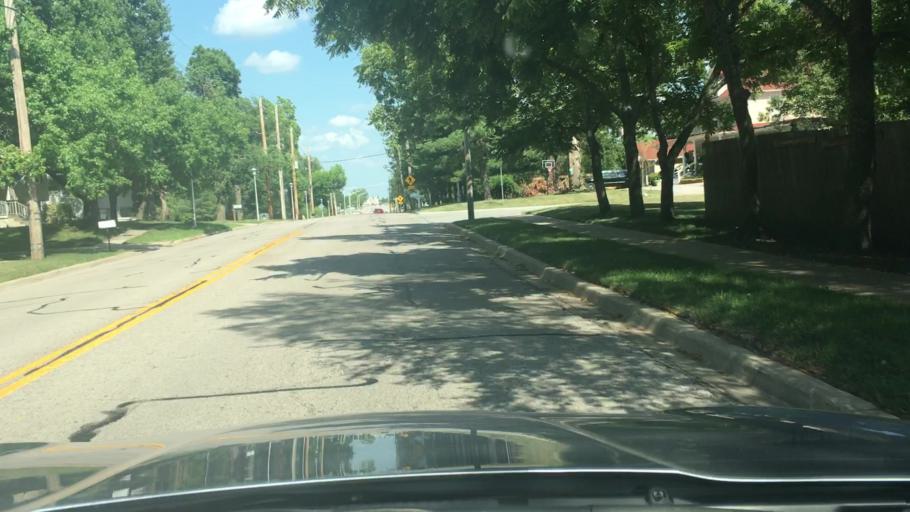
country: US
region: Missouri
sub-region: Jackson County
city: Lees Summit
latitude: 38.8963
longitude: -94.3831
